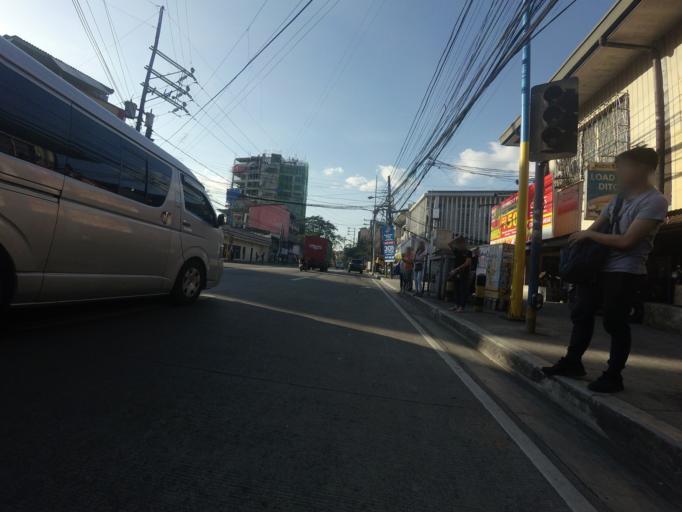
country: PH
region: Metro Manila
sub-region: Mandaluyong
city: Mandaluyong City
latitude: 14.5896
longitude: 121.0352
